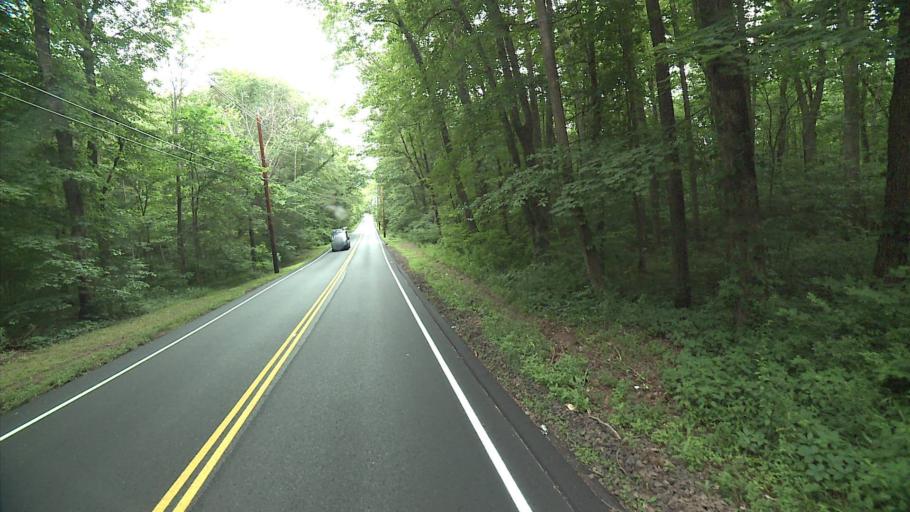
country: US
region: Connecticut
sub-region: New Haven County
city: Wallingford Center
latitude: 41.4108
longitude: -72.7980
